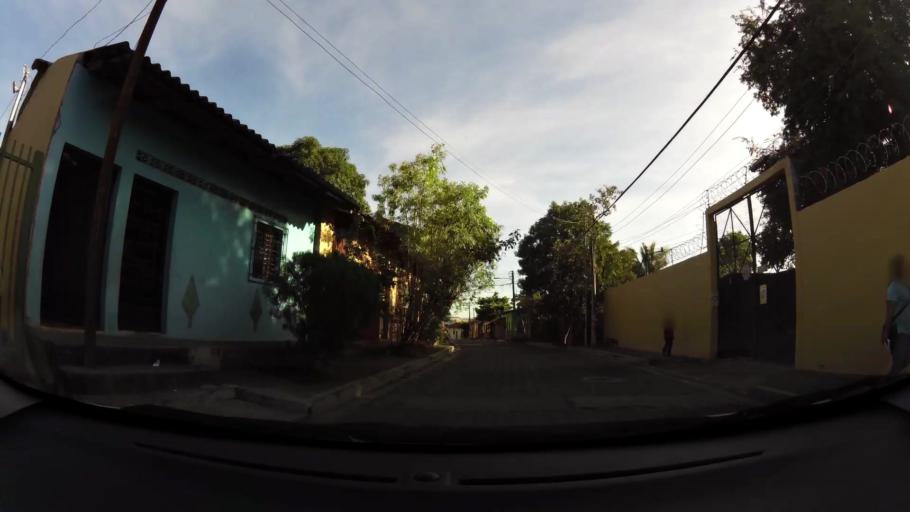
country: SV
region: San Miguel
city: San Miguel
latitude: 13.4662
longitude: -88.1777
